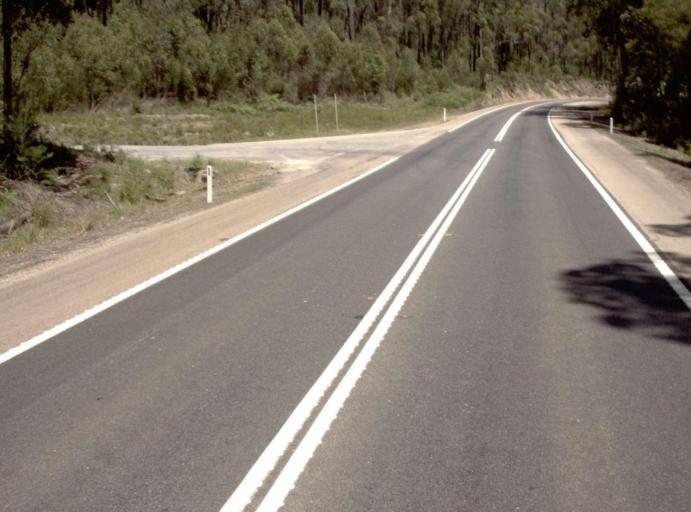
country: AU
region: New South Wales
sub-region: Bombala
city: Bombala
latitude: -37.6046
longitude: 148.9046
